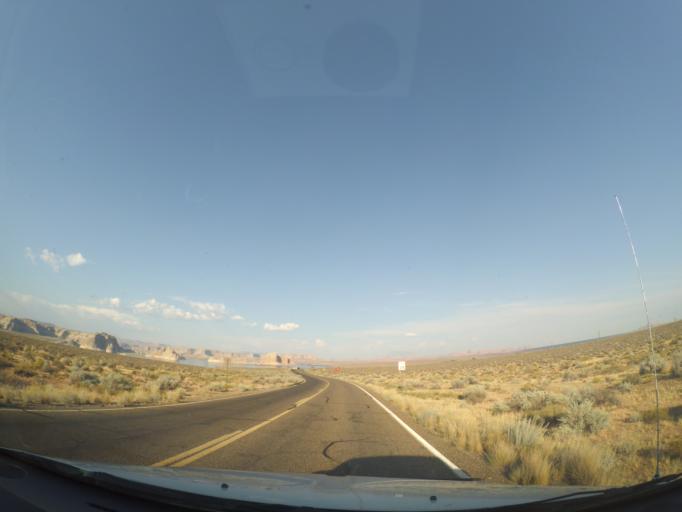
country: US
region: Arizona
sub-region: Coconino County
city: Page
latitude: 36.9929
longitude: -111.5066
